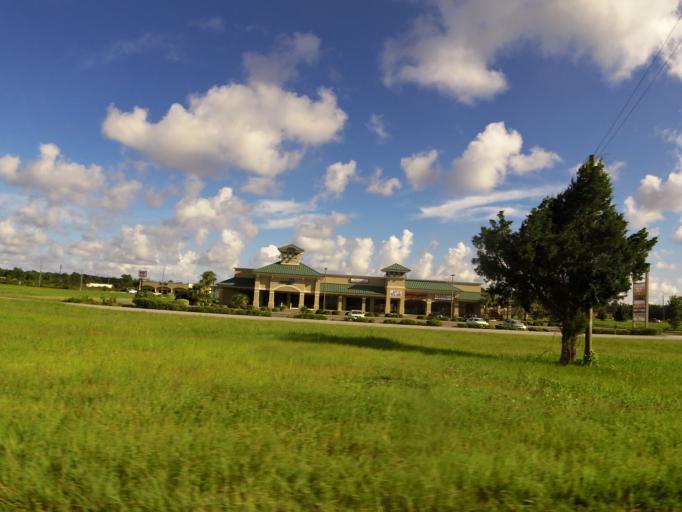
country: US
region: Georgia
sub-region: Glynn County
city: Dock Junction
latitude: 31.1400
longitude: -81.5880
